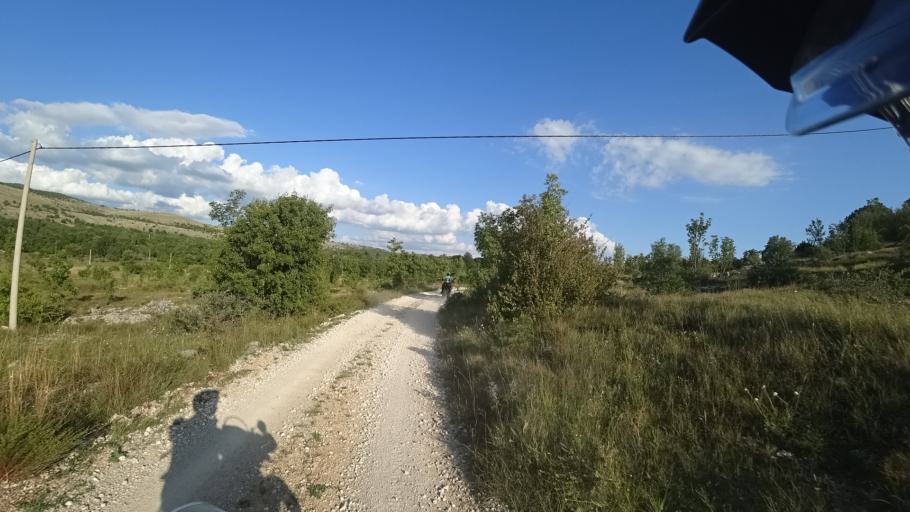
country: HR
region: Sibensko-Kniniska
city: Knin
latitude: 44.1642
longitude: 16.0903
